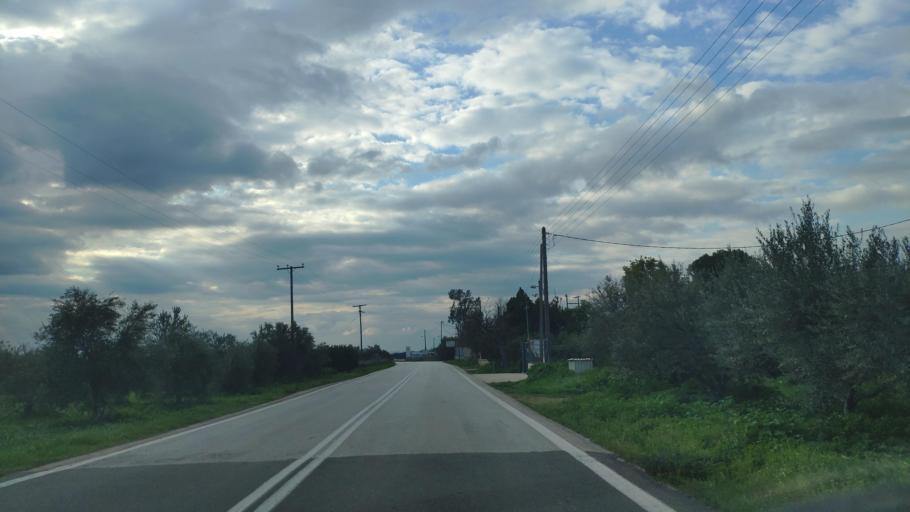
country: GR
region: Peloponnese
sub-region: Nomos Argolidos
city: Koutsopodi
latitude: 37.7159
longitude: 22.7250
